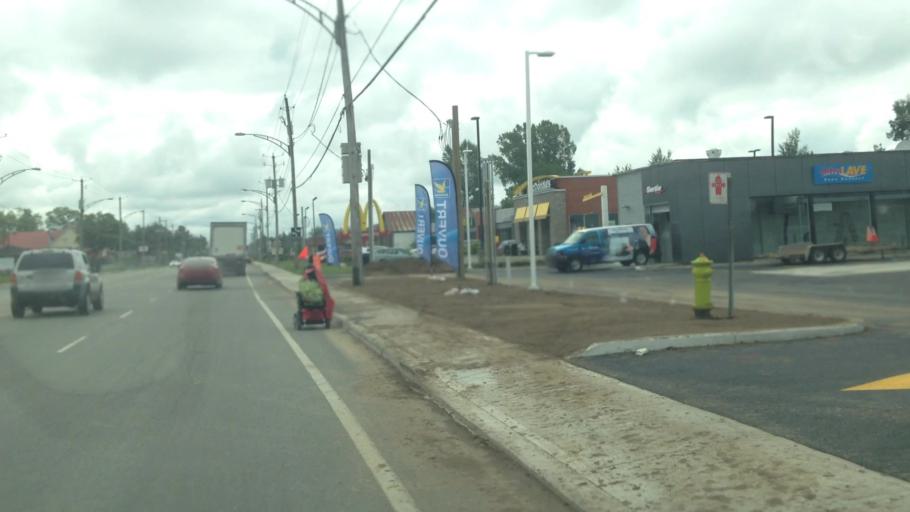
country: CA
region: Quebec
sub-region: Laurentides
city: Blainville
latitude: 45.6987
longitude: -73.9194
